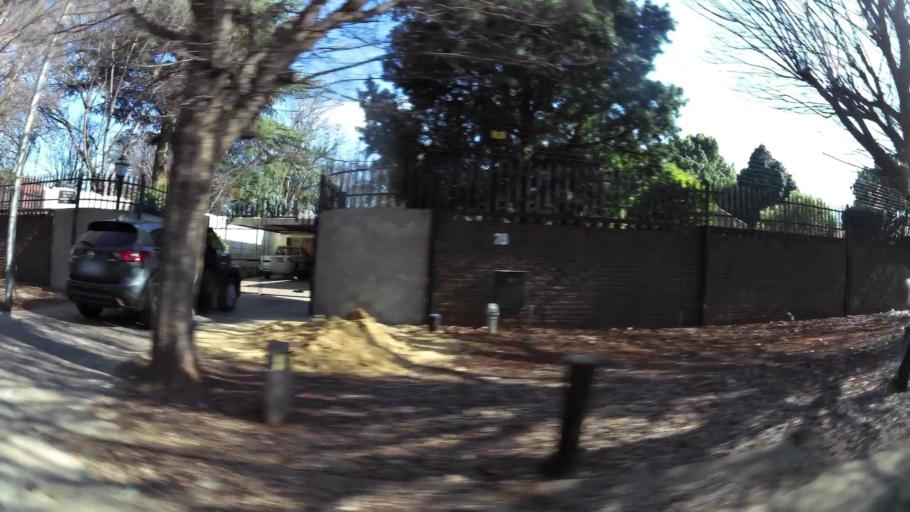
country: ZA
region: Gauteng
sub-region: Ekurhuleni Metropolitan Municipality
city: Benoni
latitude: -26.1542
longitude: 28.3346
